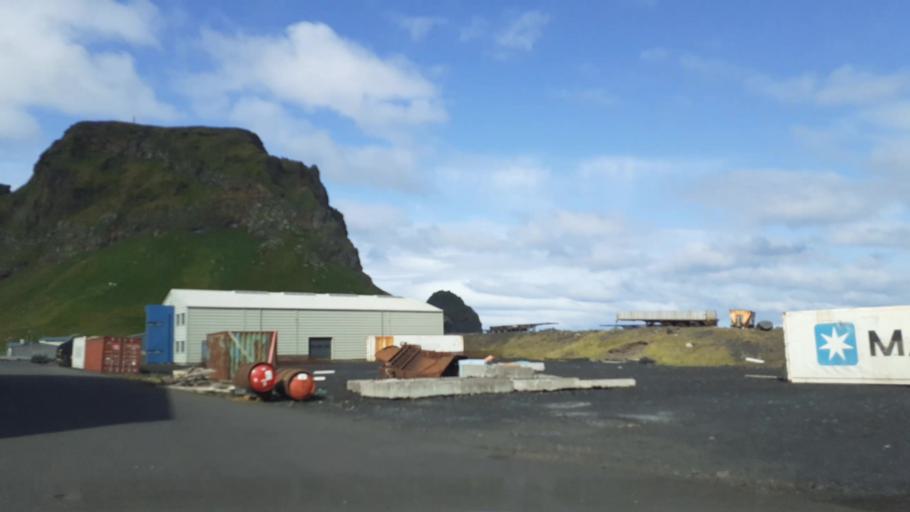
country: IS
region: South
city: Vestmannaeyjar
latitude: 63.4474
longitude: -20.2709
